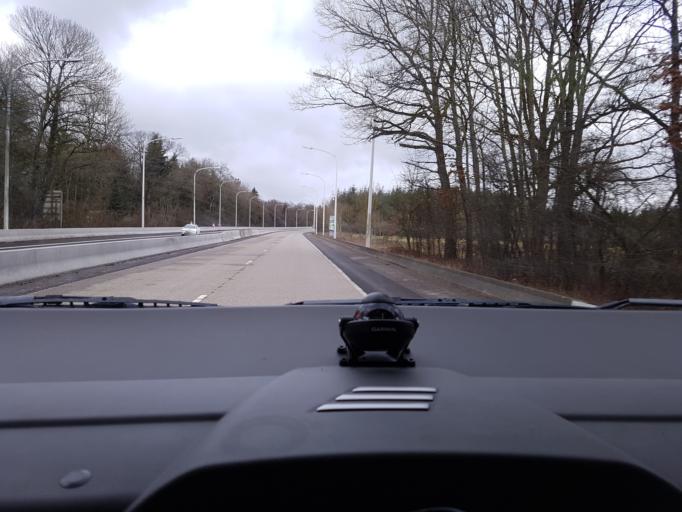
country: BE
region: Wallonia
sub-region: Province du Luxembourg
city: Marche-en-Famenne
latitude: 50.2526
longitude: 5.2772
